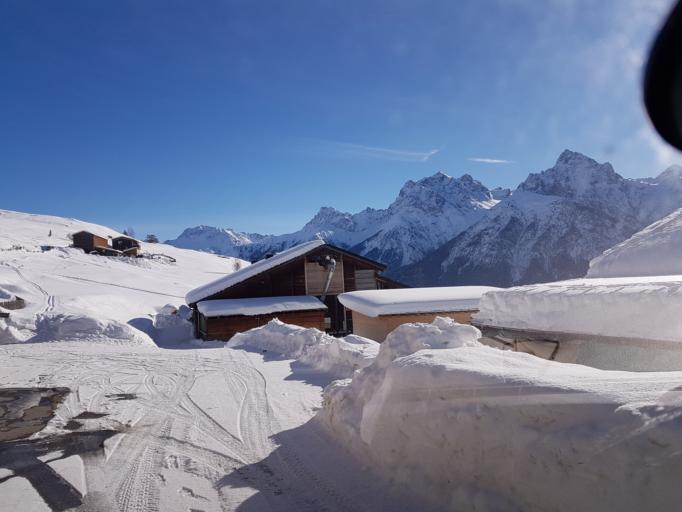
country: CH
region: Grisons
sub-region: Inn District
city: Scuol
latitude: 46.7959
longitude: 10.2549
